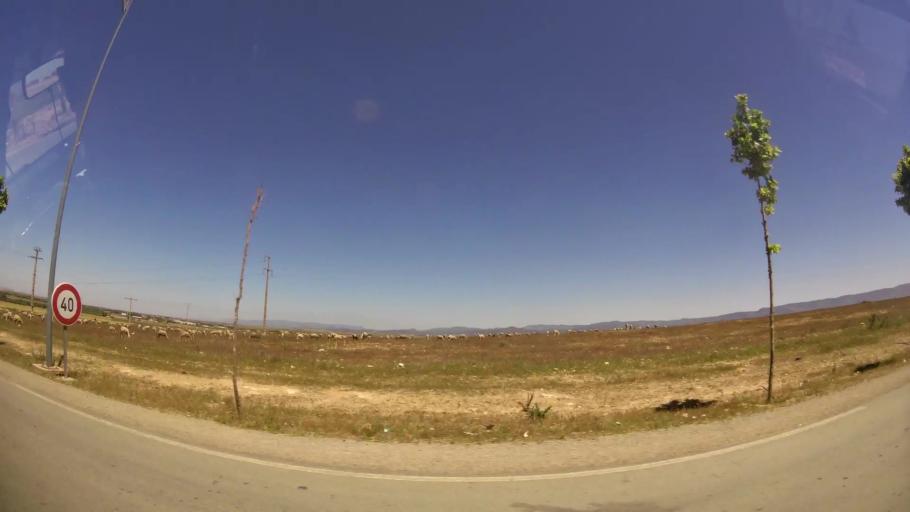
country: MA
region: Oriental
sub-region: Oujda-Angad
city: Oujda
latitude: 34.6868
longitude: -1.8575
